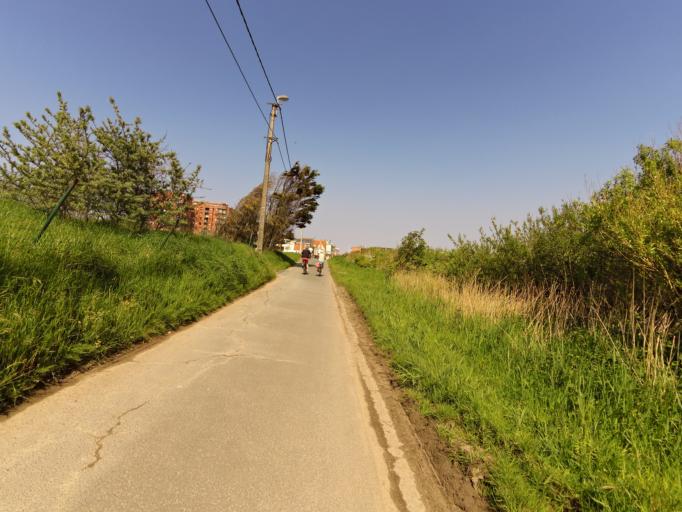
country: BE
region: Flanders
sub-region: Provincie West-Vlaanderen
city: Middelkerke
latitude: 51.2050
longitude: 2.8571
